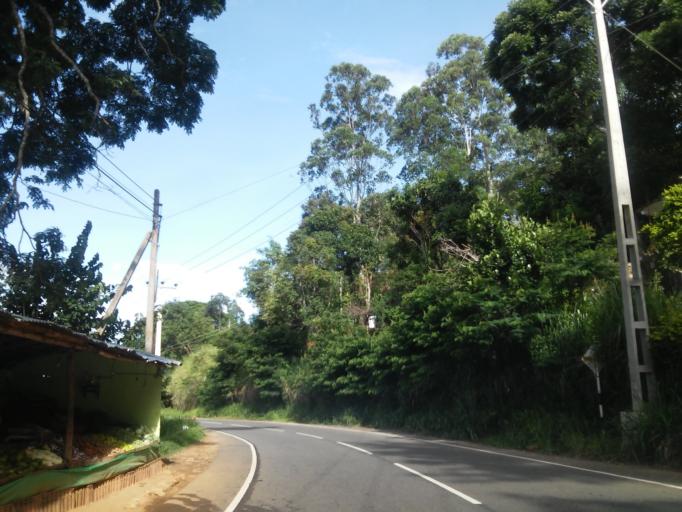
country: LK
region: Uva
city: Haputale
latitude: 6.7632
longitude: 80.9050
